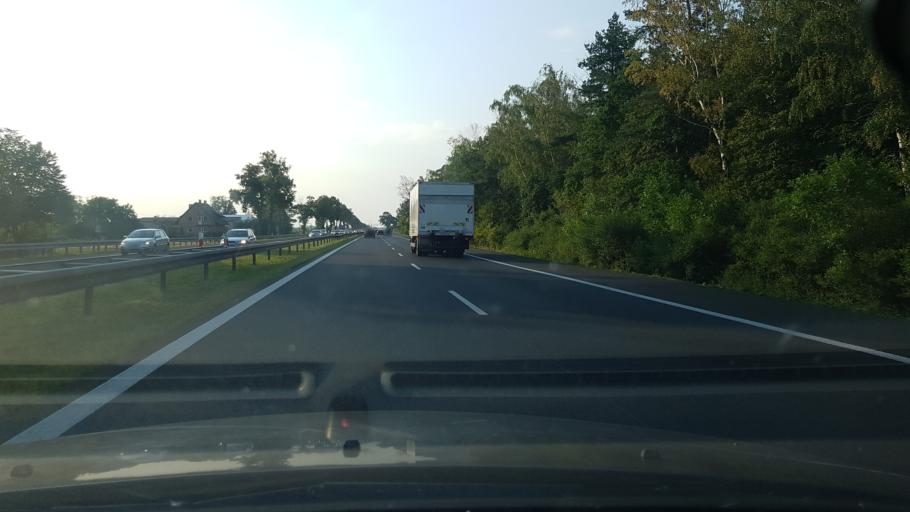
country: PL
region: Masovian Voivodeship
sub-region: Powiat nowodworski
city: Zakroczym
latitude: 52.4563
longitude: 20.5800
